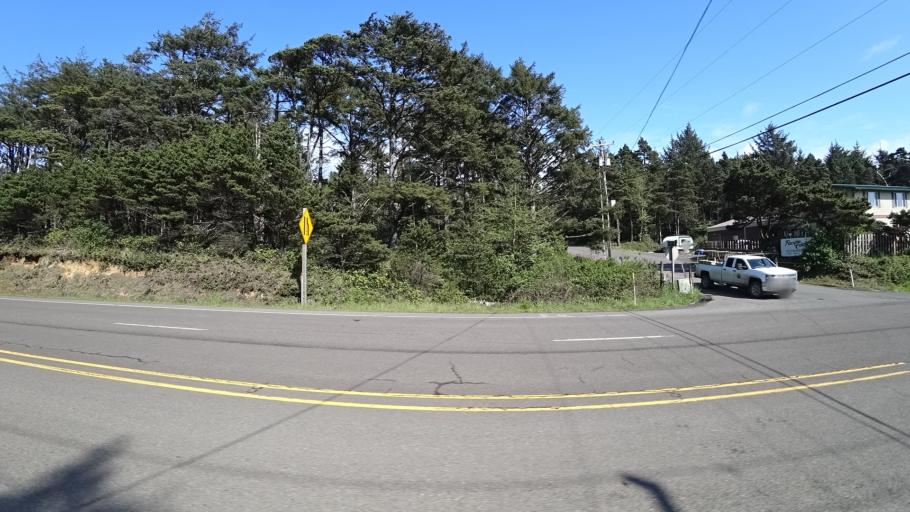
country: US
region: Oregon
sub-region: Lincoln County
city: Newport
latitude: 44.5681
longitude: -124.0685
